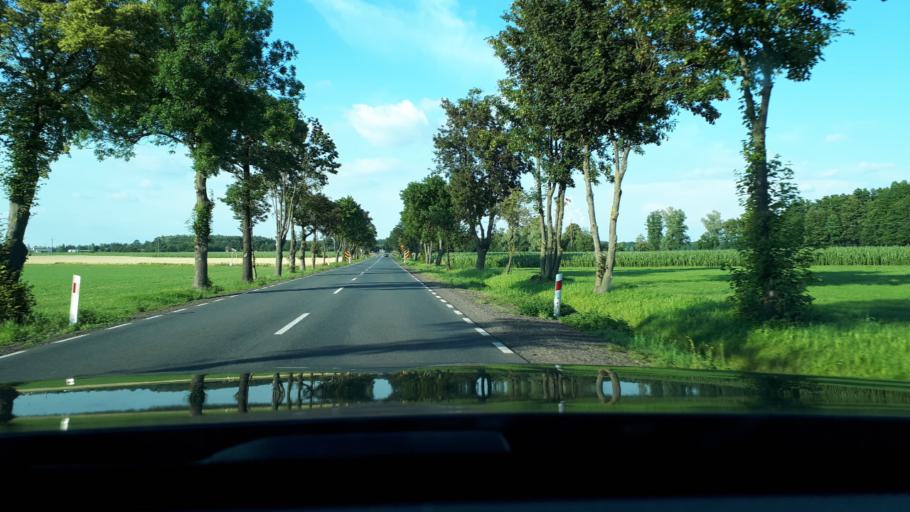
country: PL
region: Masovian Voivodeship
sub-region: Powiat ciechanowski
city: Ojrzen
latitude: 52.8055
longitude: 20.6008
